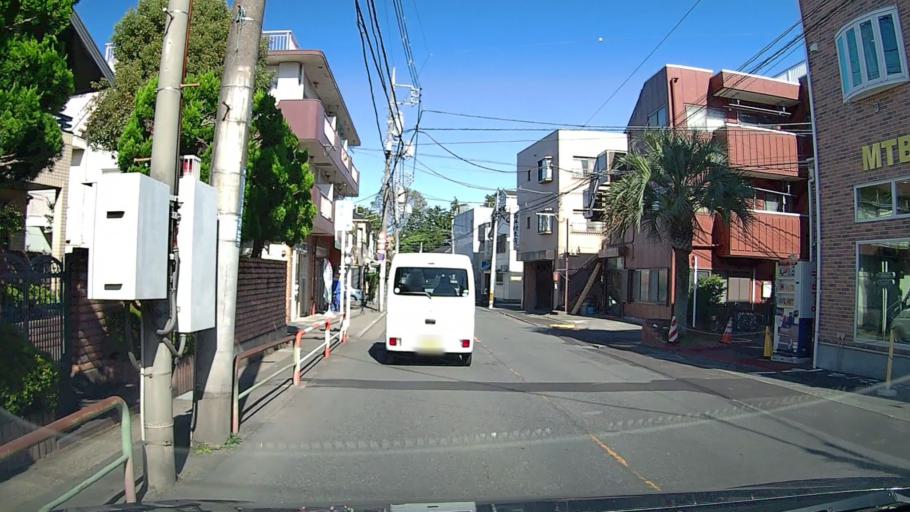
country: JP
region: Saitama
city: Wako
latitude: 35.7728
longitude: 139.6250
